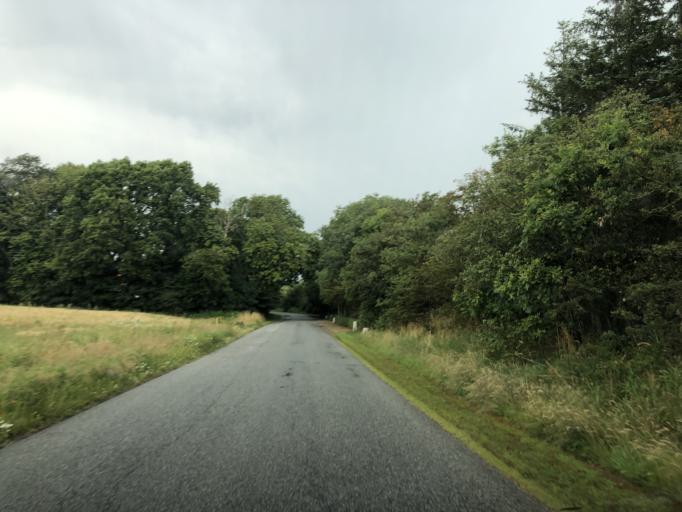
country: DK
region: Central Jutland
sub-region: Ringkobing-Skjern Kommune
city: Skjern
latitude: 55.8995
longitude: 8.4421
